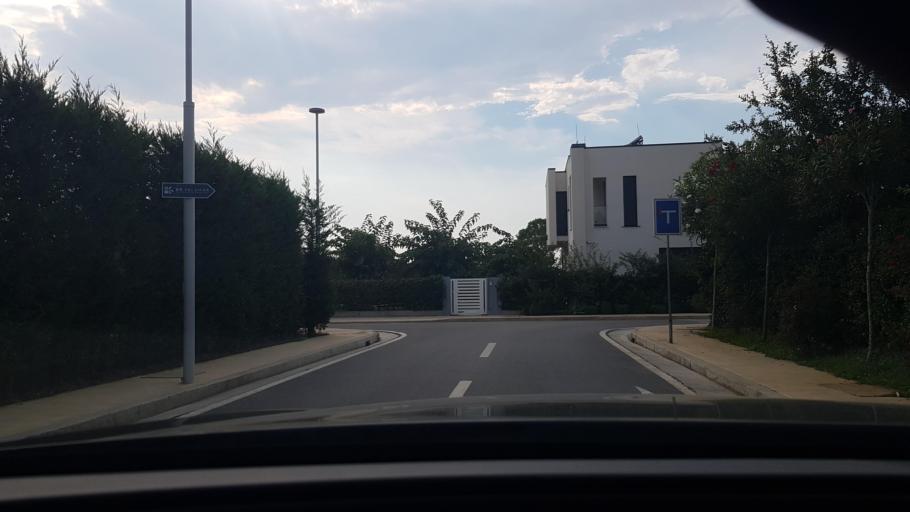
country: AL
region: Durres
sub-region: Rrethi i Durresit
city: Katundi i Ri
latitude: 41.4900
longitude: 19.5120
